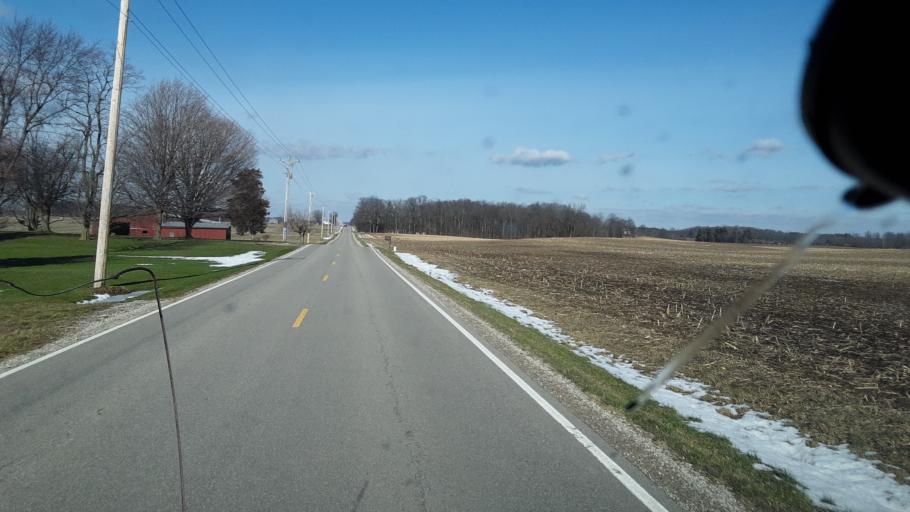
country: US
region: Ohio
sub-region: Huron County
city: Plymouth
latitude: 40.9533
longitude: -82.7432
